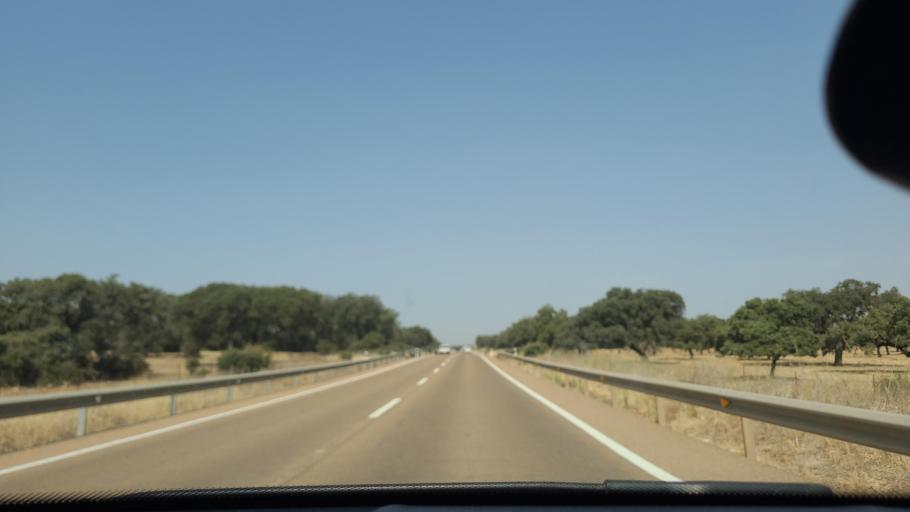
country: ES
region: Extremadura
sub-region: Provincia de Badajoz
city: Usagre
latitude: 38.3674
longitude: -6.2386
